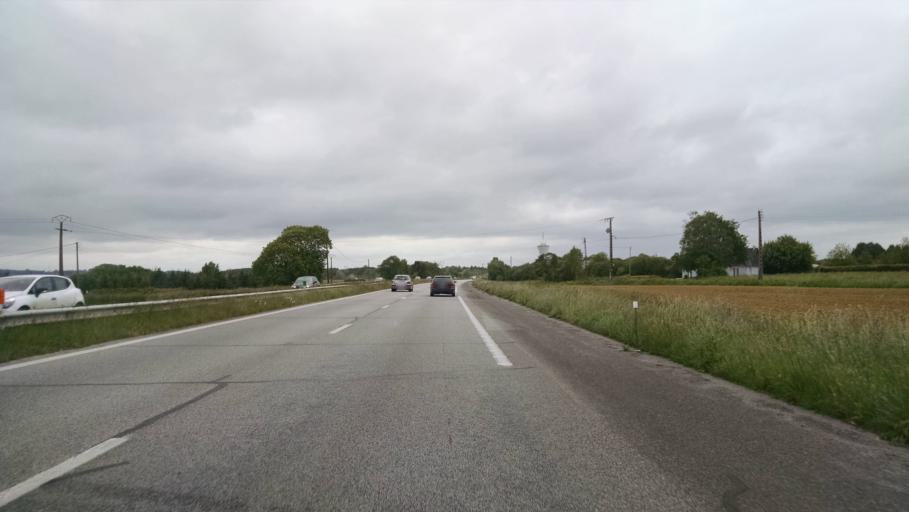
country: FR
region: Brittany
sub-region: Departement du Finistere
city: Landrevarzec
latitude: 48.0843
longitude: -4.0424
